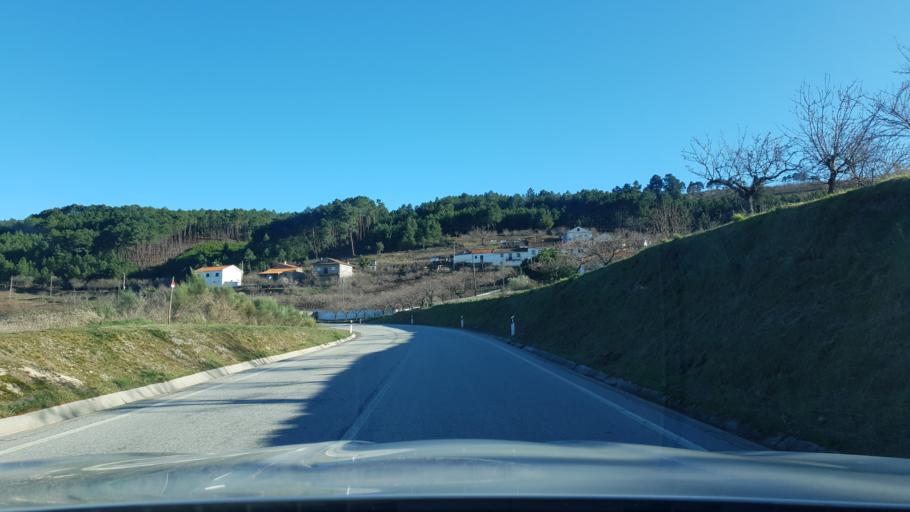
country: PT
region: Braganca
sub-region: Freixo de Espada A Cinta
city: Freixo de Espada a Cinta
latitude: 41.1803
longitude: -6.8210
